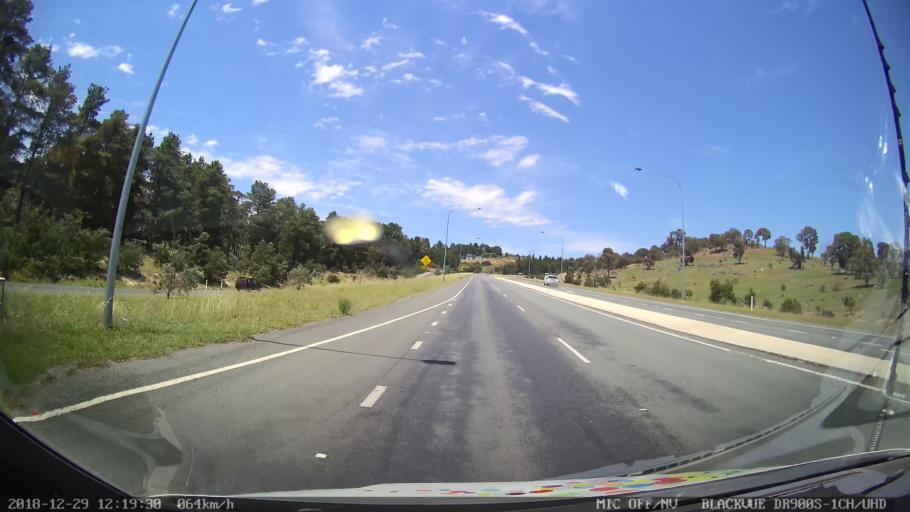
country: AU
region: New South Wales
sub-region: Queanbeyan
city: Queanbeyan
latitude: -35.3944
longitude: 149.2334
